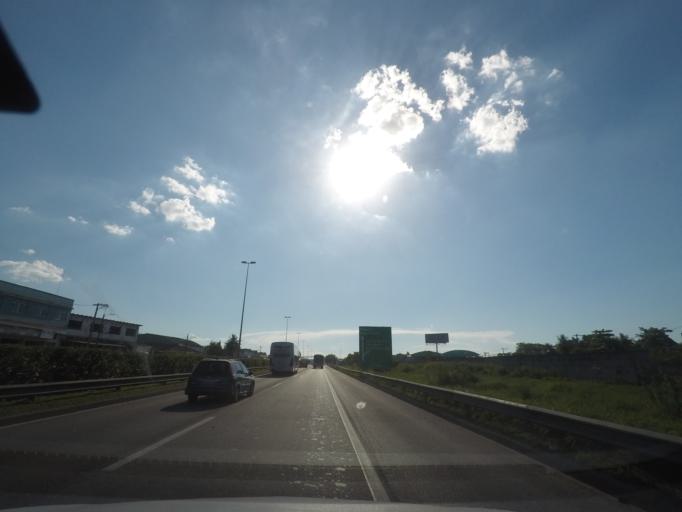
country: BR
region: Rio de Janeiro
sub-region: Duque De Caxias
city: Duque de Caxias
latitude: -22.6686
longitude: -43.2695
